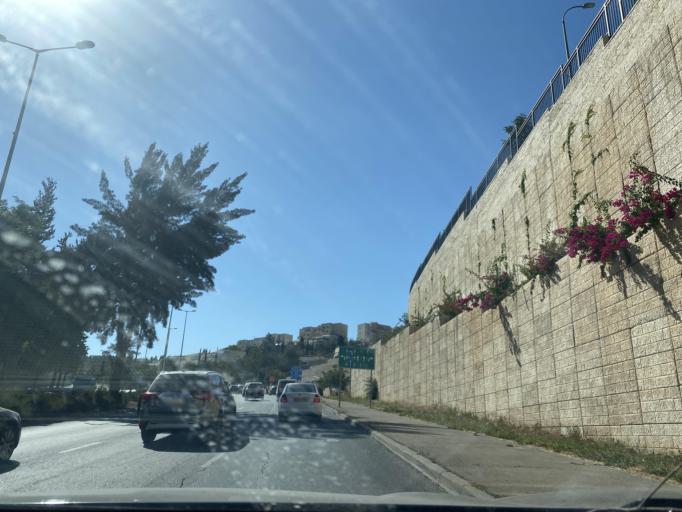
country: PS
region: West Bank
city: Bayt Iksa
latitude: 31.8118
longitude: 35.2027
